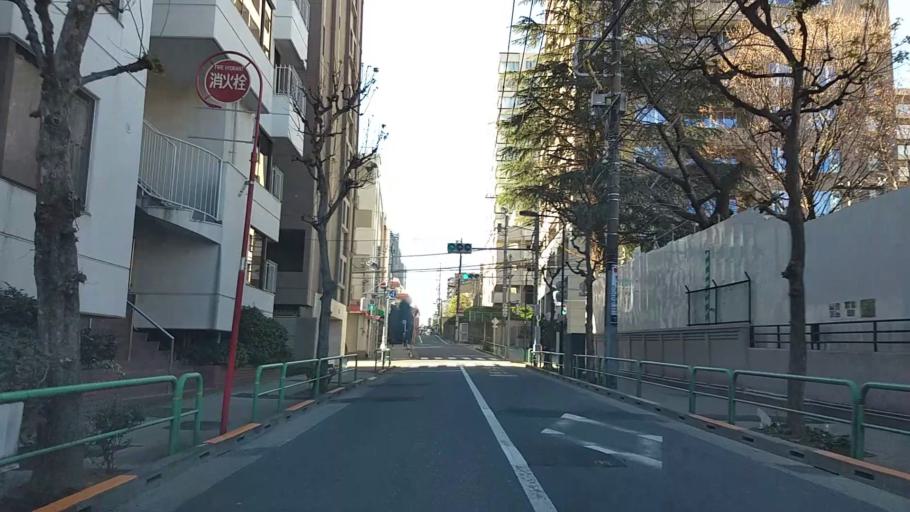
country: JP
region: Tokyo
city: Tokyo
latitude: 35.6899
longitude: 139.7404
